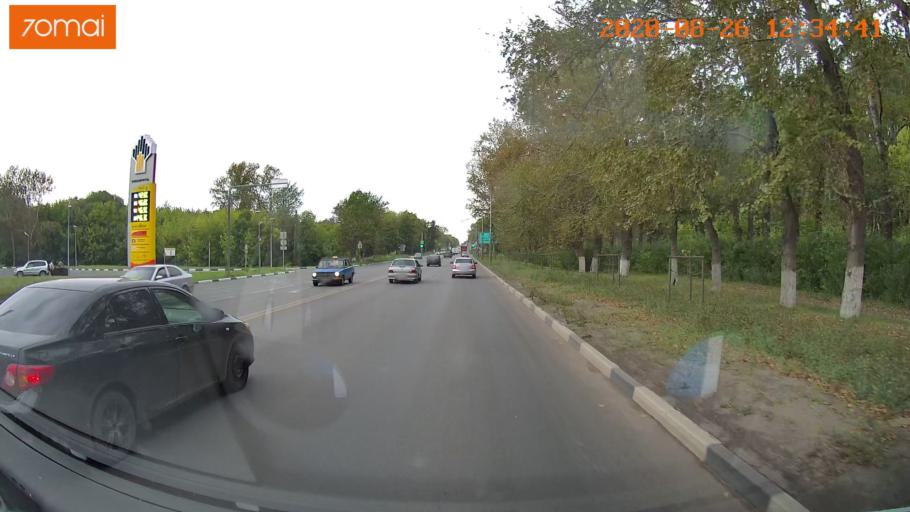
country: RU
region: Rjazan
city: Ryazan'
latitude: 54.5899
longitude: 39.7707
